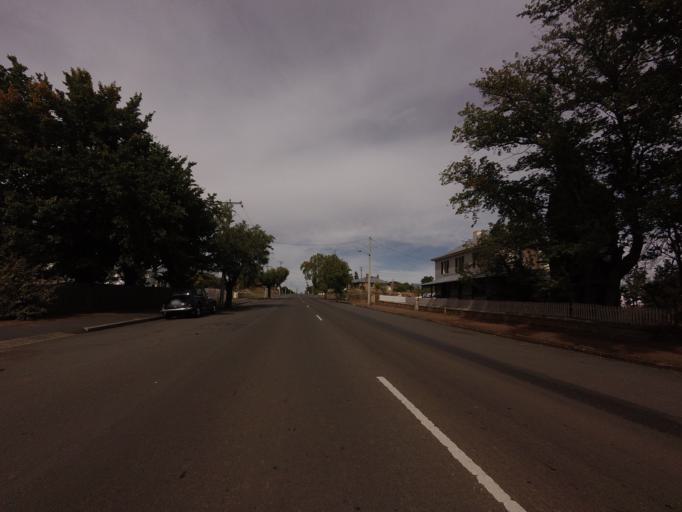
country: AU
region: Tasmania
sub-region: Brighton
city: Bridgewater
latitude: -42.3021
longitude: 147.3682
